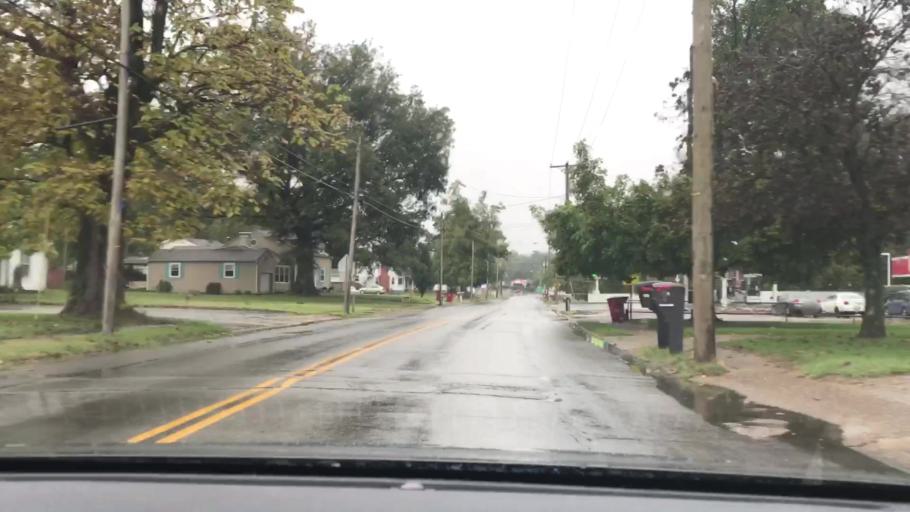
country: US
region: Kentucky
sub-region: McLean County
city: Calhoun
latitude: 37.5435
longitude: -87.2595
